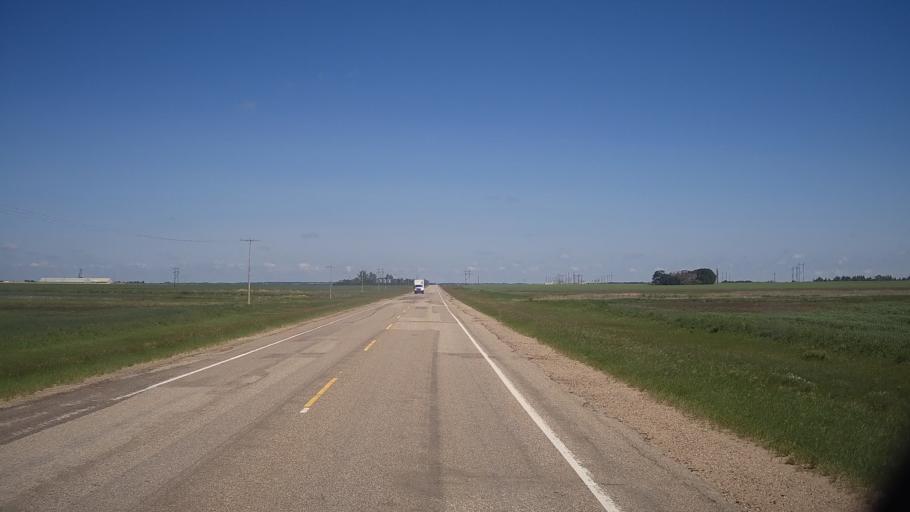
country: CA
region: Saskatchewan
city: Saskatoon
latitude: 51.9715
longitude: -106.0753
